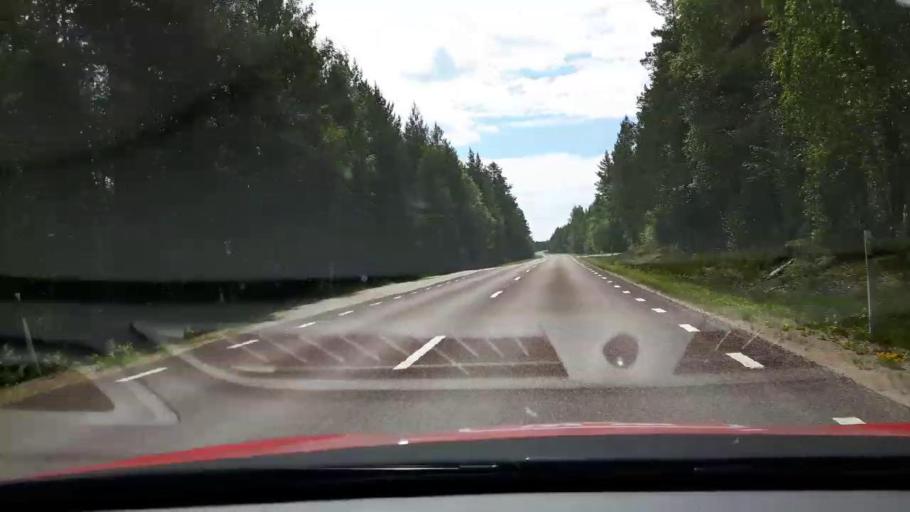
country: SE
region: Jaemtland
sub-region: Harjedalens Kommun
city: Sveg
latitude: 62.1135
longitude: 14.9704
